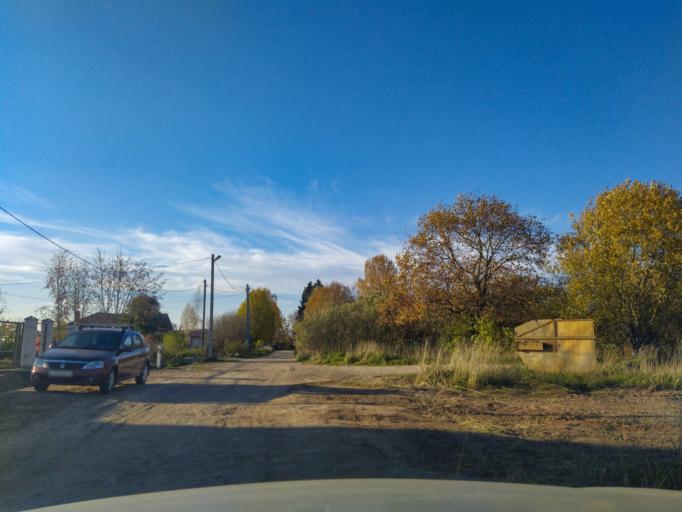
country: RU
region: Leningrad
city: Siverskiy
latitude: 59.3228
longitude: 30.0468
